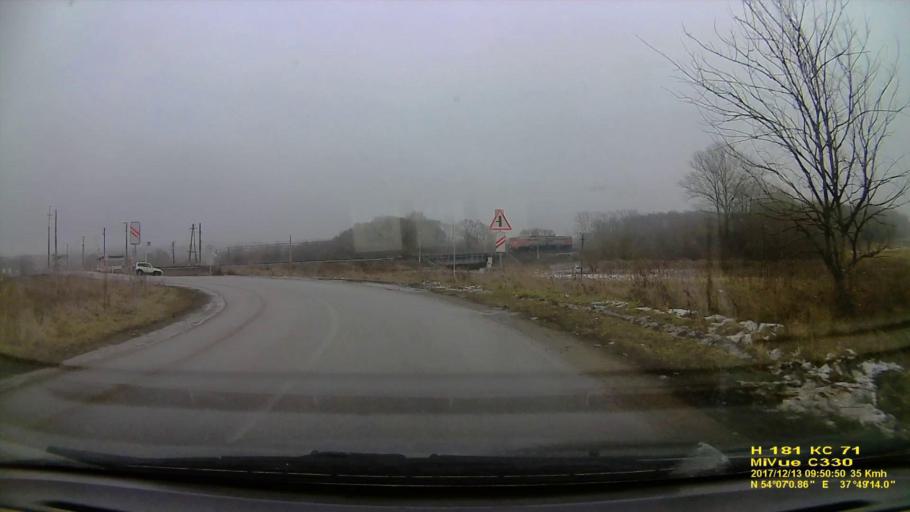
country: RU
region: Tula
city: Bolokhovo
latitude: 54.1170
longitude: 37.8207
